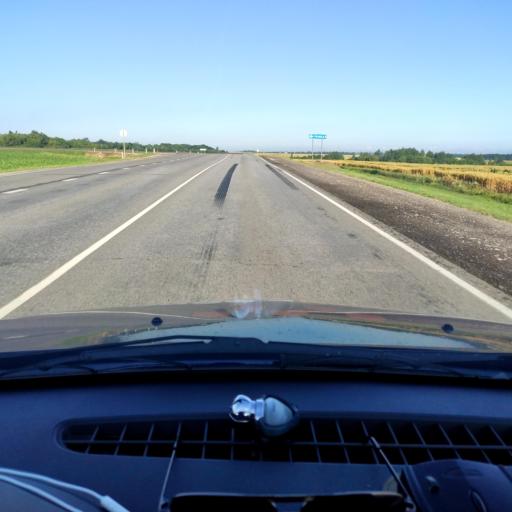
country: RU
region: Orjol
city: Livny
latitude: 52.4328
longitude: 37.3551
